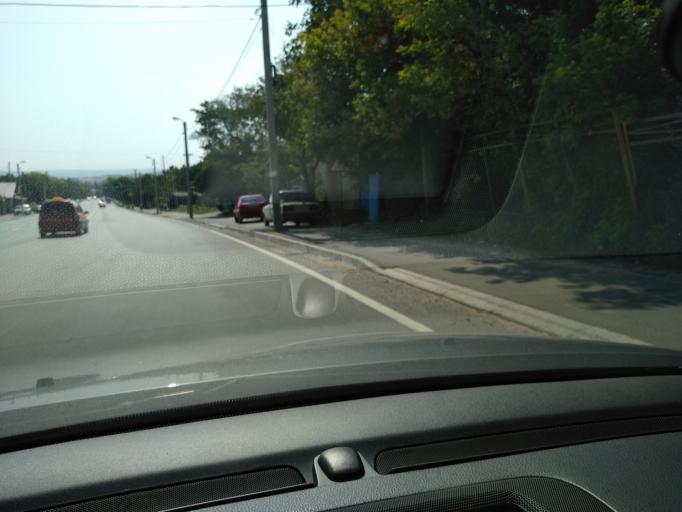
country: MD
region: Chisinau
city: Cricova
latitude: 47.2473
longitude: 28.7619
